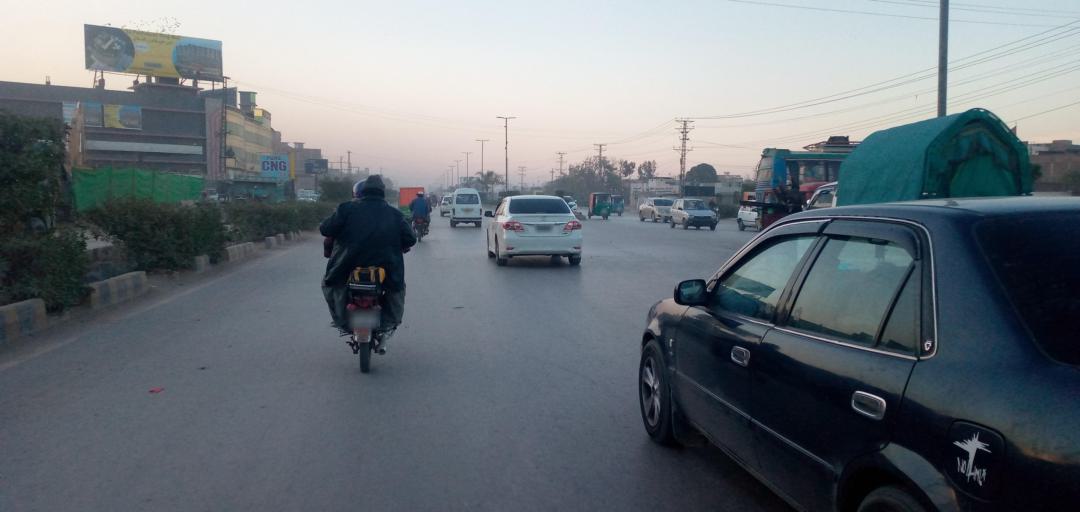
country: PK
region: Khyber Pakhtunkhwa
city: Peshawar
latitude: 34.0290
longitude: 71.6142
